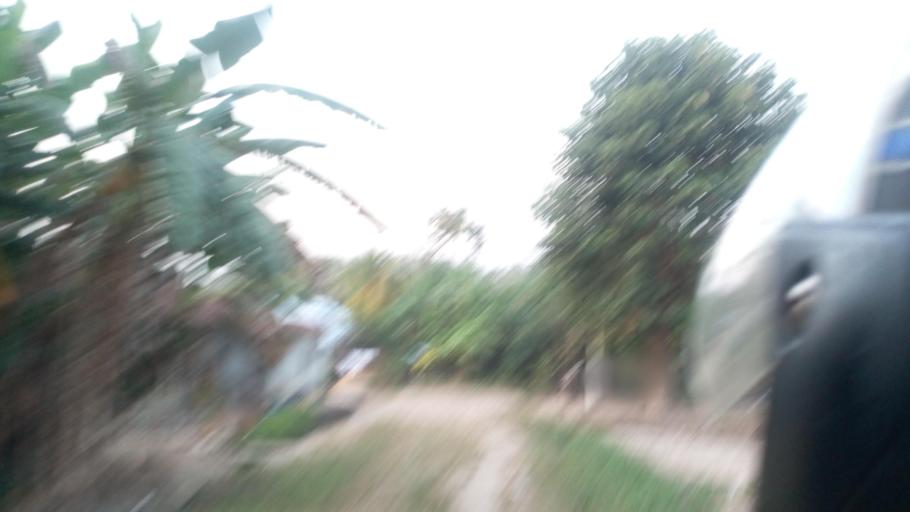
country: SL
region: Southern Province
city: Mogbwemo
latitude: 7.6079
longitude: -12.1713
